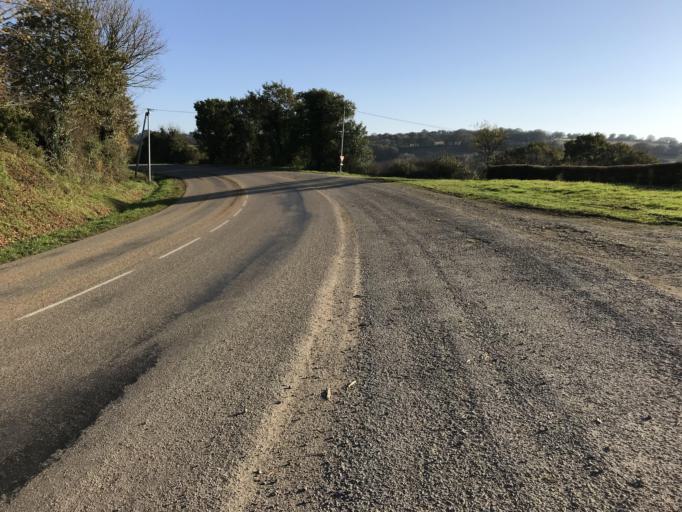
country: FR
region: Brittany
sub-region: Departement du Finistere
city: Hopital-Camfrout
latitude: 48.3154
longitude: -4.2288
